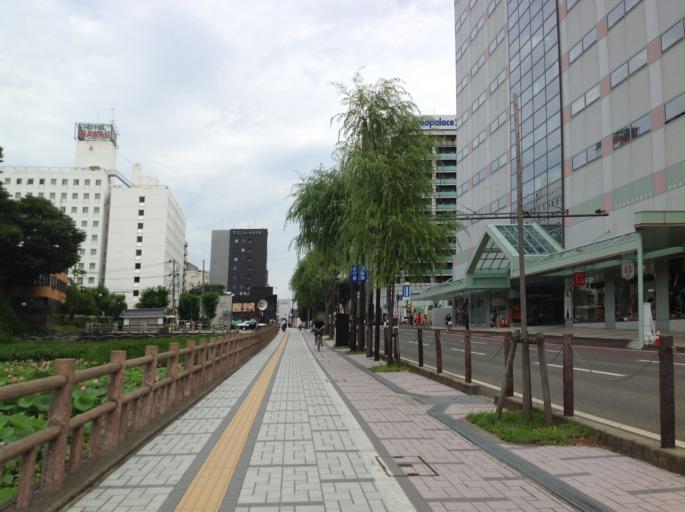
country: JP
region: Akita
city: Akita
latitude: 39.7180
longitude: 140.1240
